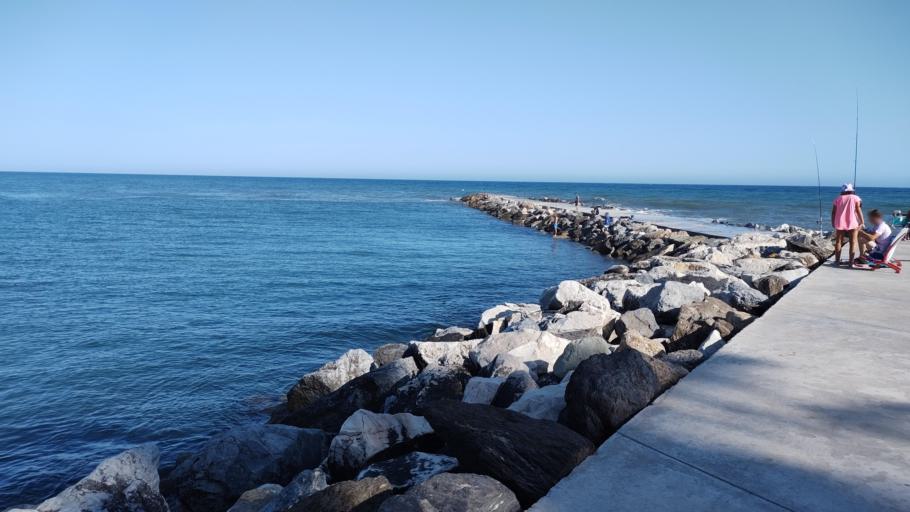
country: ES
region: Andalusia
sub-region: Provincia de Malaga
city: Benalmadena
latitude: 36.5796
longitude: -4.5398
